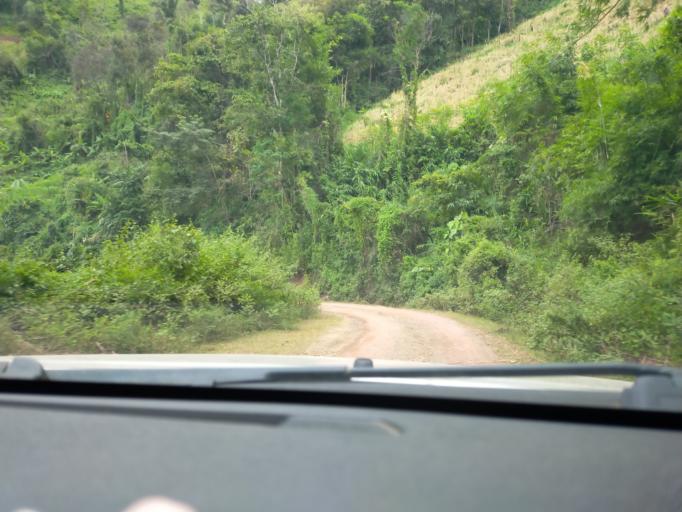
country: TH
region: Nan
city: Chaloem Phra Kiat
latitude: 19.7744
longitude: 101.3506
